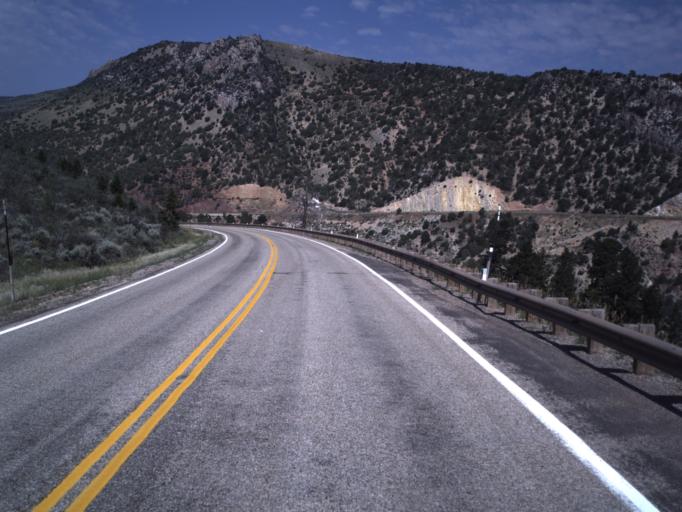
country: US
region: Utah
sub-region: Daggett County
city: Manila
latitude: 40.8911
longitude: -109.7106
